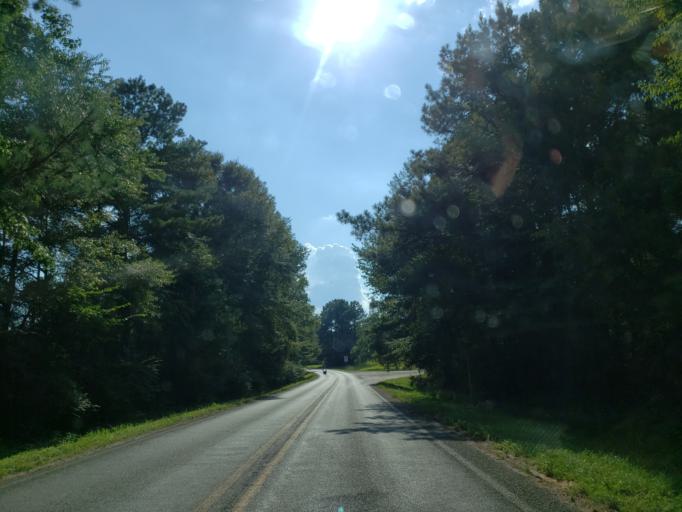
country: US
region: Mississippi
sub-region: Jones County
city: Sharon
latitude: 31.9197
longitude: -89.0369
